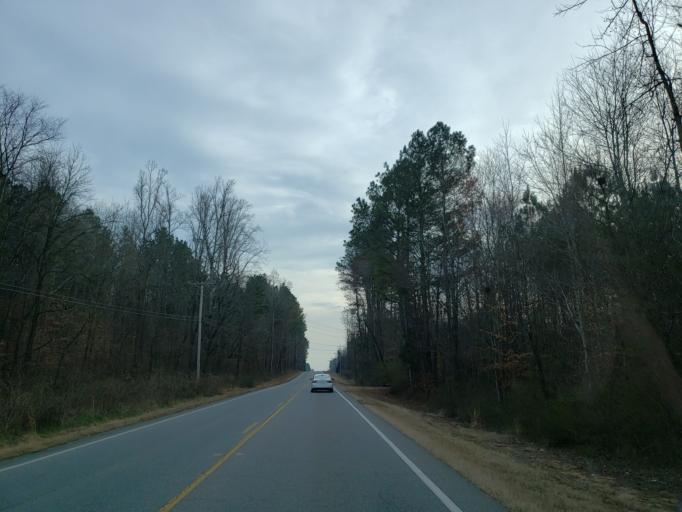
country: US
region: Georgia
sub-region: Whitfield County
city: Varnell
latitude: 34.9722
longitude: -84.9347
